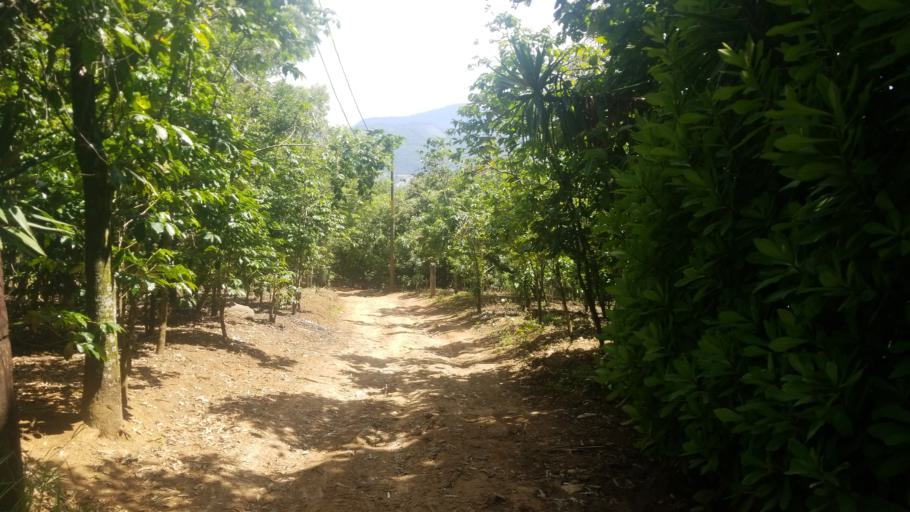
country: GT
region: Guatemala
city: Amatitlan
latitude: 14.5023
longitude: -90.6447
